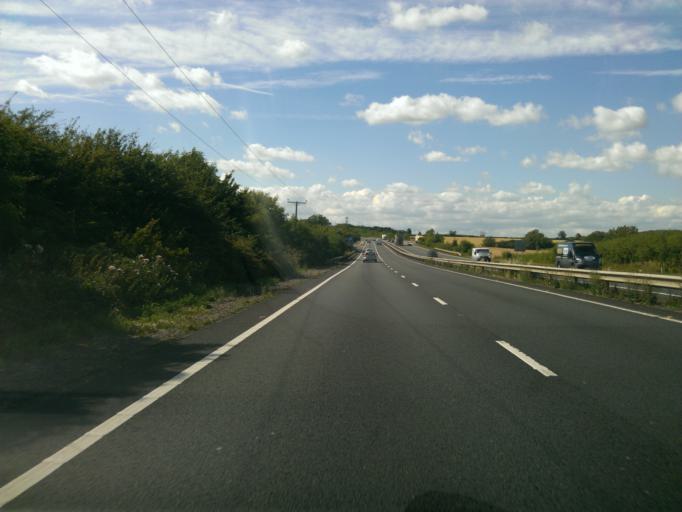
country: GB
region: England
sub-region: Northamptonshire
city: Thrapston
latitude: 52.3775
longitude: -0.4716
